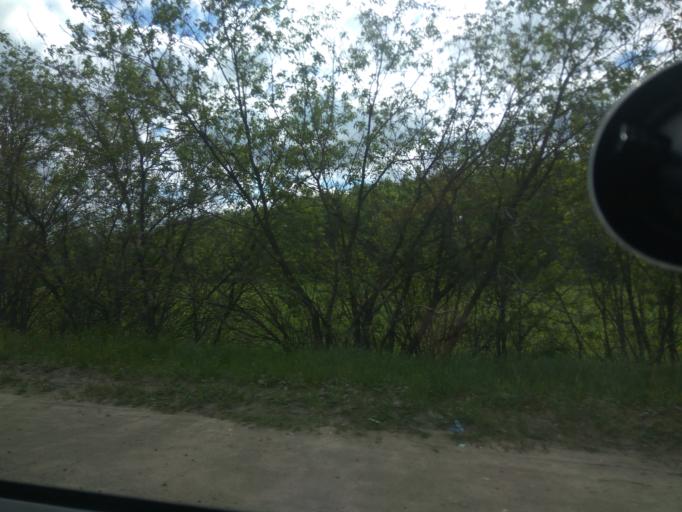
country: RU
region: Moskovskaya
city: Zhukovskiy
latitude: 55.5458
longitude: 38.0667
